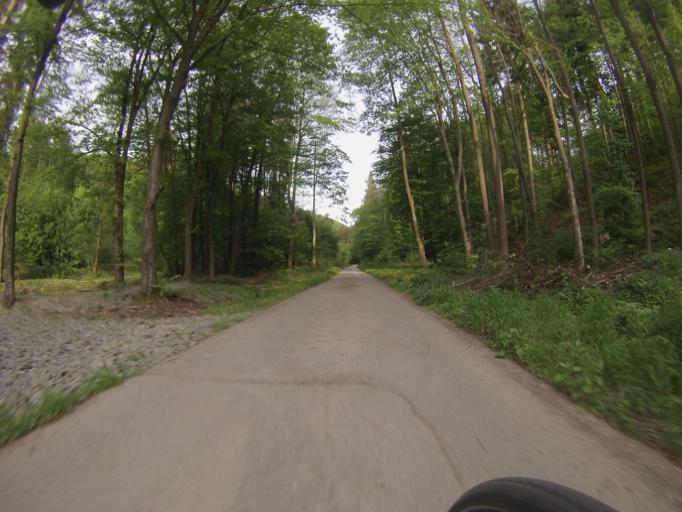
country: CZ
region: Olomoucky
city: Pteni
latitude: 49.4811
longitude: 16.9153
